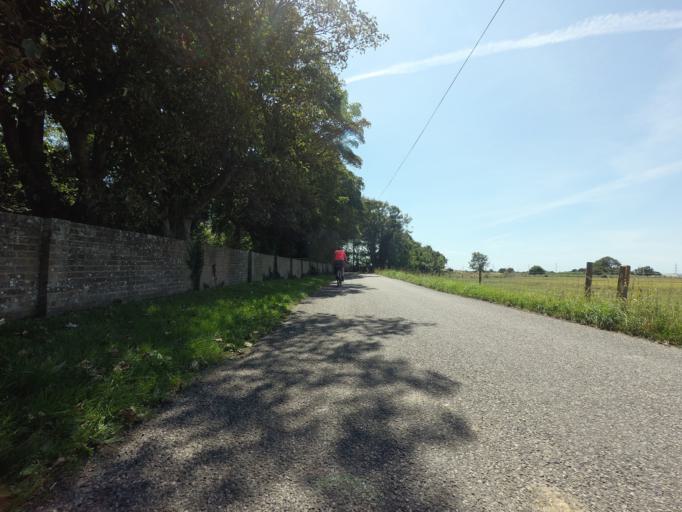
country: GB
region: England
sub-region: Kent
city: Lydd
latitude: 50.9564
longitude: 0.9036
